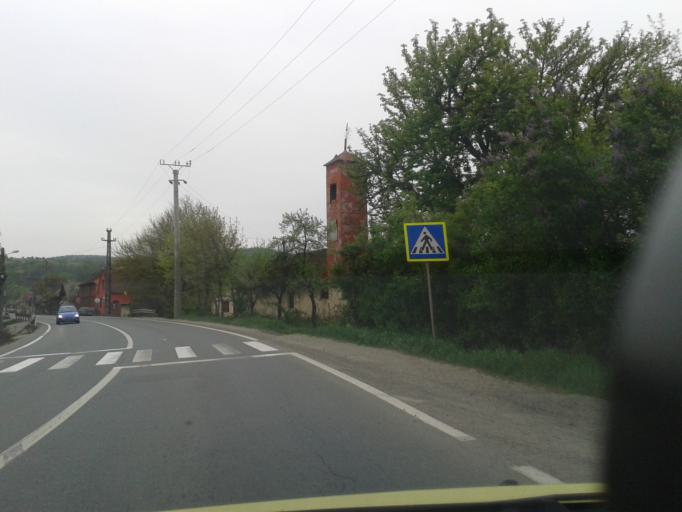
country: RO
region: Arad
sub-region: Oras Lipova
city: Radna
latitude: 46.0939
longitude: 21.6859
